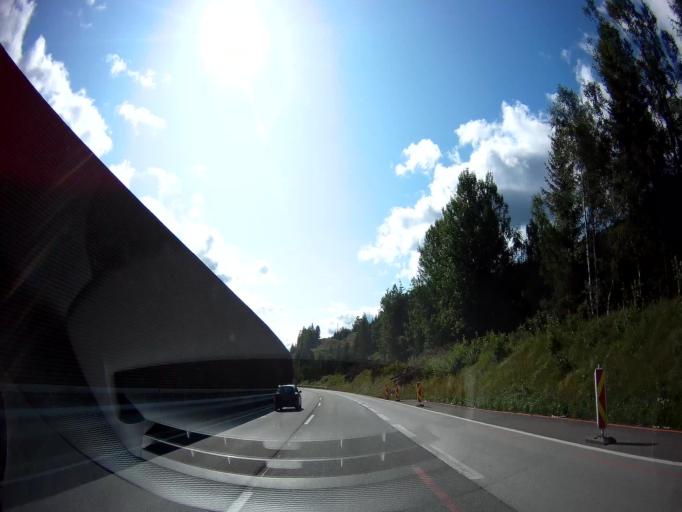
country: AT
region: Salzburg
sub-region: Politischer Bezirk Tamsweg
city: Zederhaus
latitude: 47.1283
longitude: 13.5517
